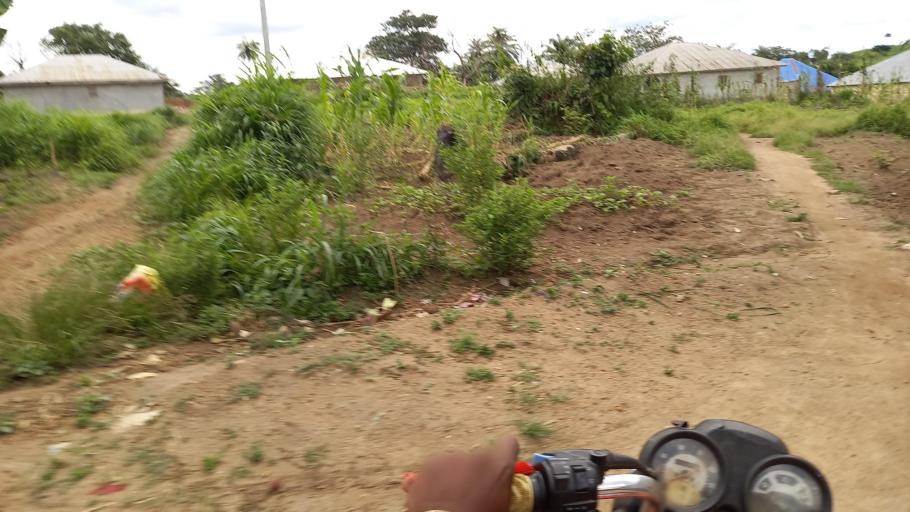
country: SL
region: Northern Province
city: Kamakwie
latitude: 9.5067
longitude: -12.2434
